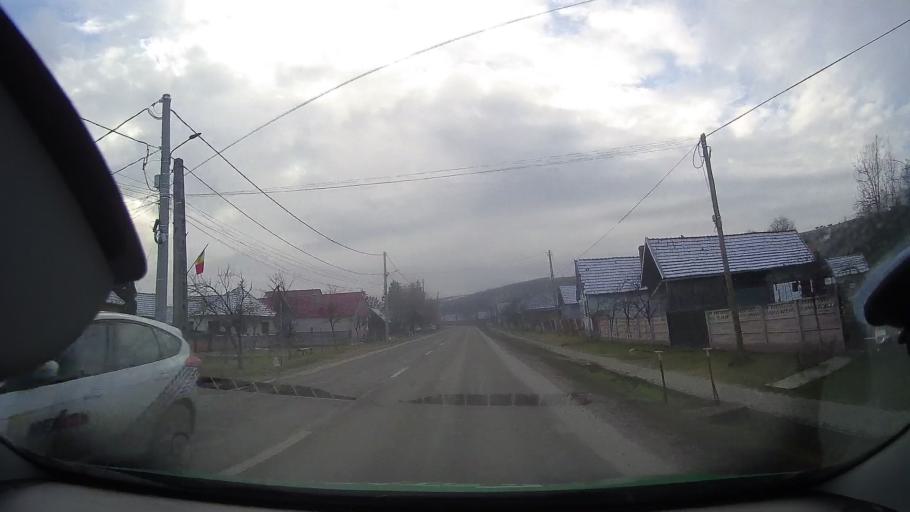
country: RO
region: Mures
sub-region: Comuna Cucerdea
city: Cucerdea
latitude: 46.4072
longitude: 24.2668
